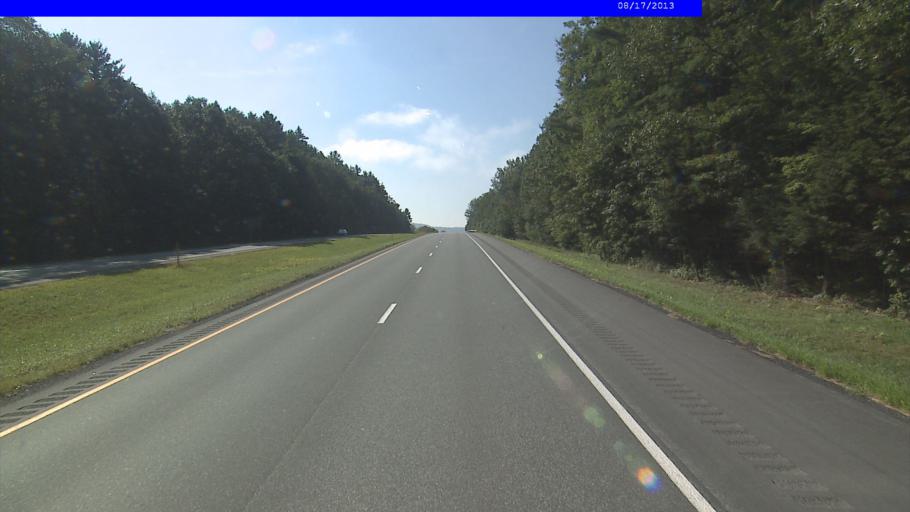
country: US
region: Vermont
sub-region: Windsor County
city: White River Junction
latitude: 43.6109
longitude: -72.3446
